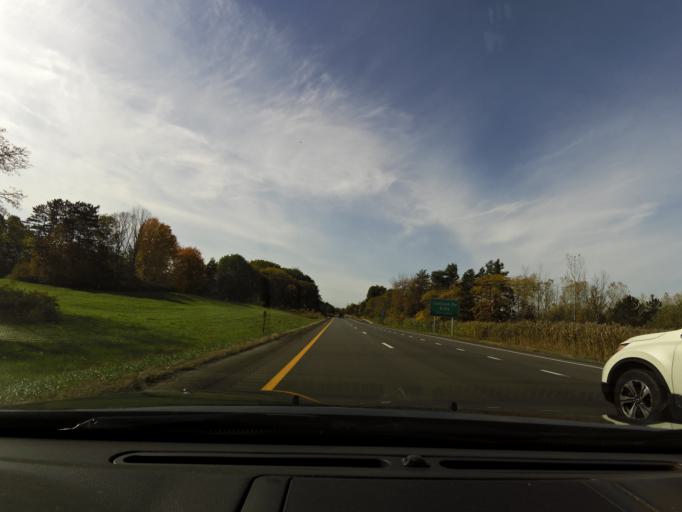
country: US
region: New York
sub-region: Erie County
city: Billington Heights
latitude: 42.7972
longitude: -78.6232
